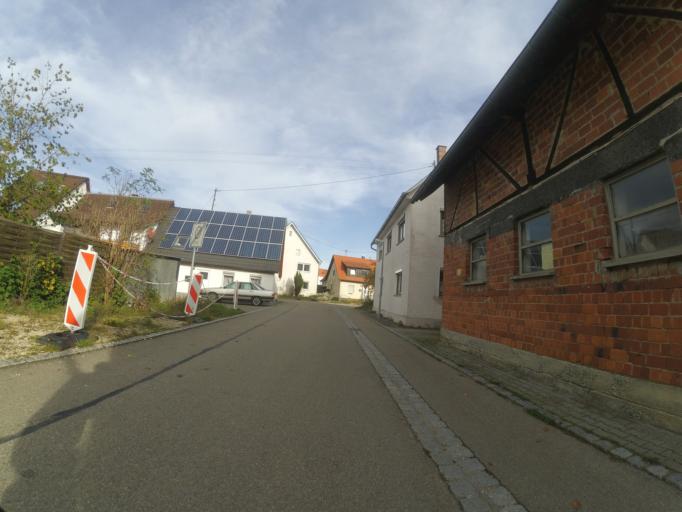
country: DE
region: Baden-Wuerttemberg
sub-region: Tuebingen Region
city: Blaubeuren
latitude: 48.4262
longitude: 9.8597
